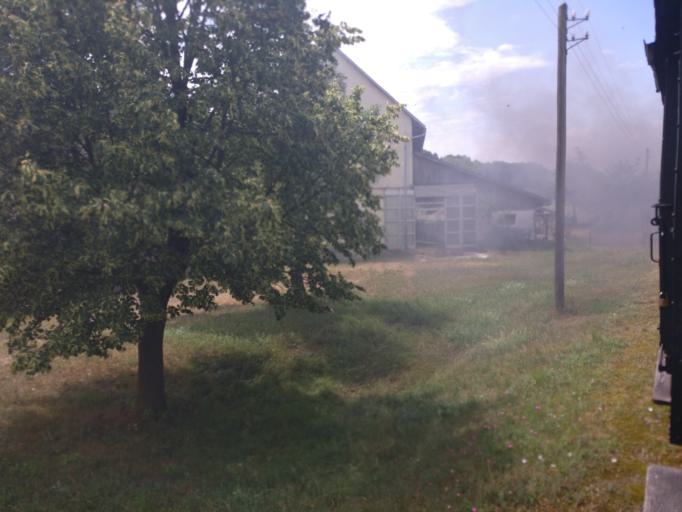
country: AT
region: Upper Austria
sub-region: Politischer Bezirk Steyr-Land
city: Sierning
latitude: 48.0173
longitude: 14.3180
